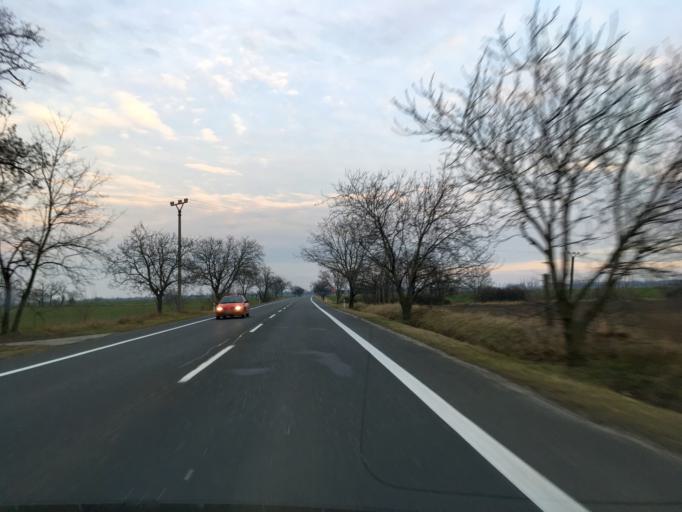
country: HU
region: Komarom-Esztergom
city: Acs
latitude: 47.7772
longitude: 17.9402
